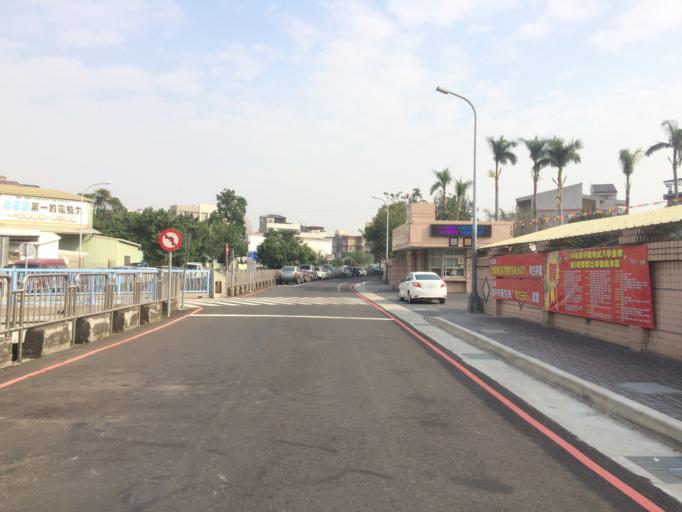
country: TW
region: Taiwan
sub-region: Taichung City
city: Taichung
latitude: 24.1796
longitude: 120.6966
